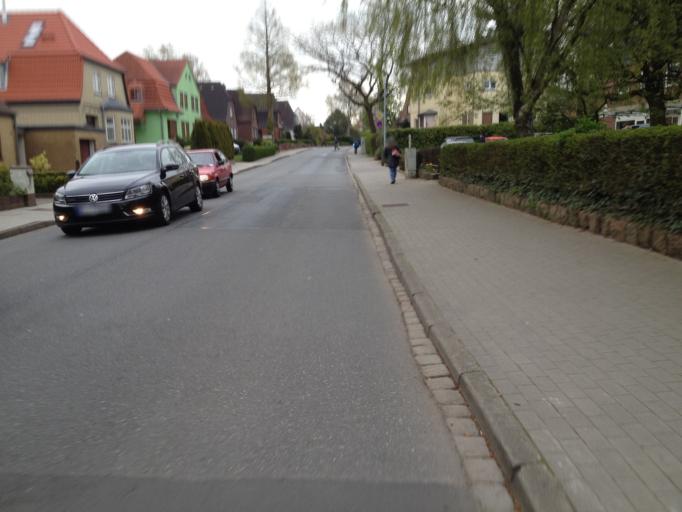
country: DE
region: Schleswig-Holstein
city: Flensburg
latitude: 54.7815
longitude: 9.4531
